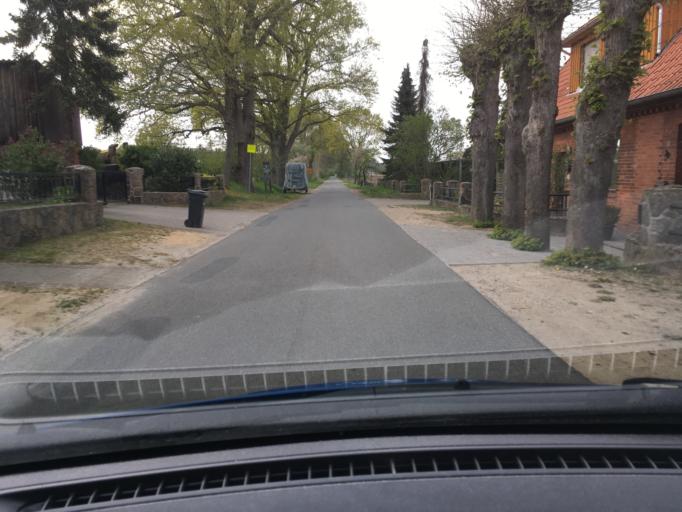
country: DE
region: Lower Saxony
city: Neetze
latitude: 53.2684
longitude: 10.6164
